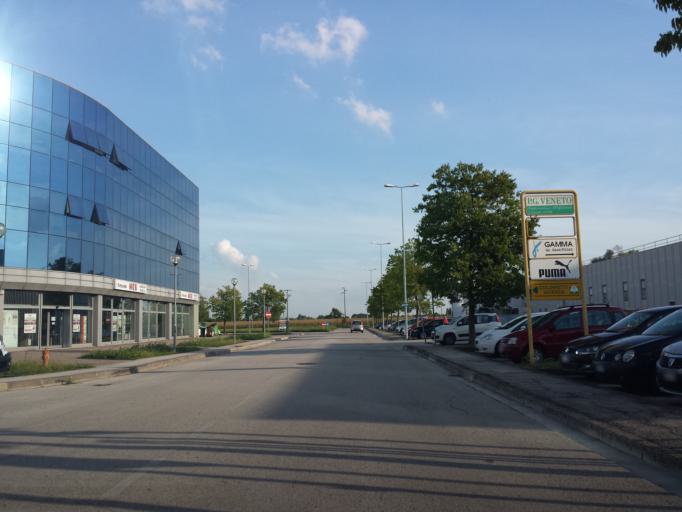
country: IT
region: Veneto
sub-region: Provincia di Vicenza
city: Villaggio Montegrappa
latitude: 45.5245
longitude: 11.5901
